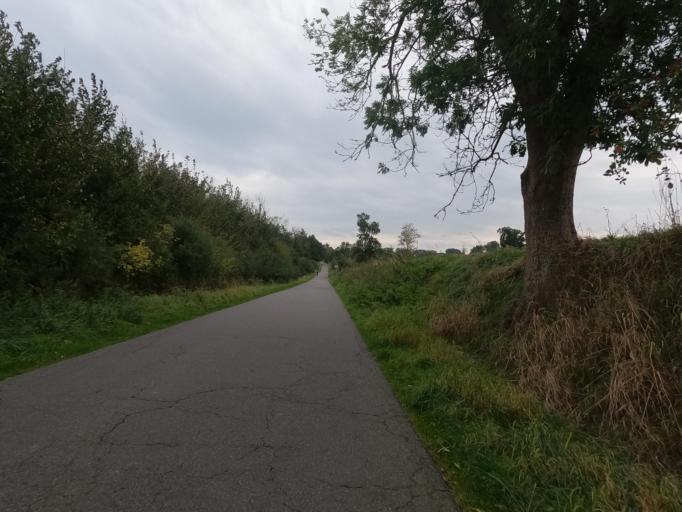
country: DE
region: Schleswig-Holstein
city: Neukirchen
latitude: 54.3037
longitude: 11.0463
